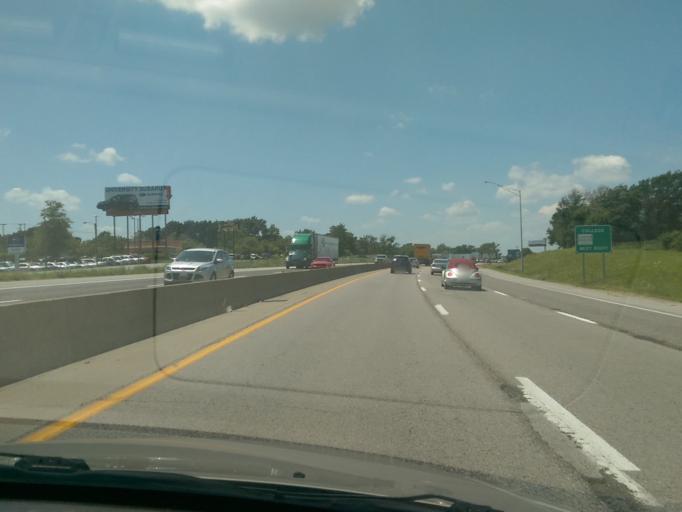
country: US
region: Missouri
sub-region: Boone County
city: Columbia
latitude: 38.9648
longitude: -92.3560
